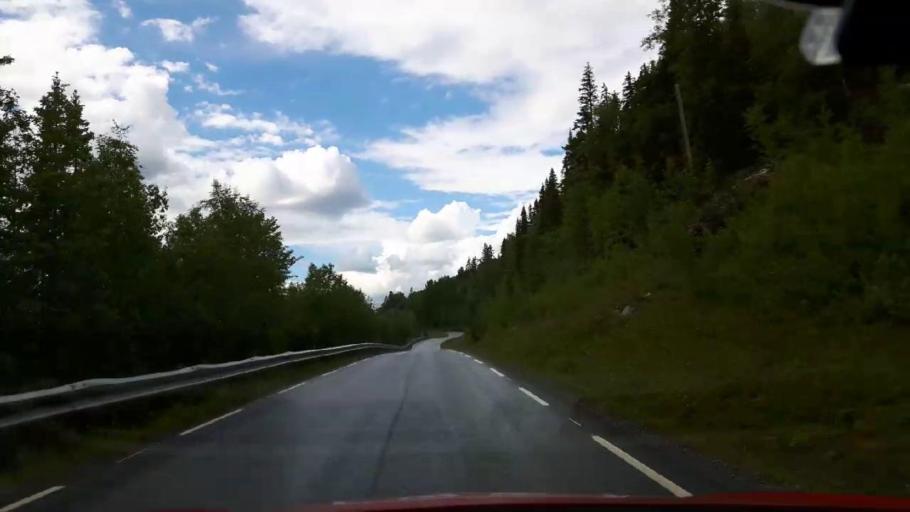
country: NO
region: Nord-Trondelag
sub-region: Lierne
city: Sandvika
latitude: 64.1044
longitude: 13.9949
